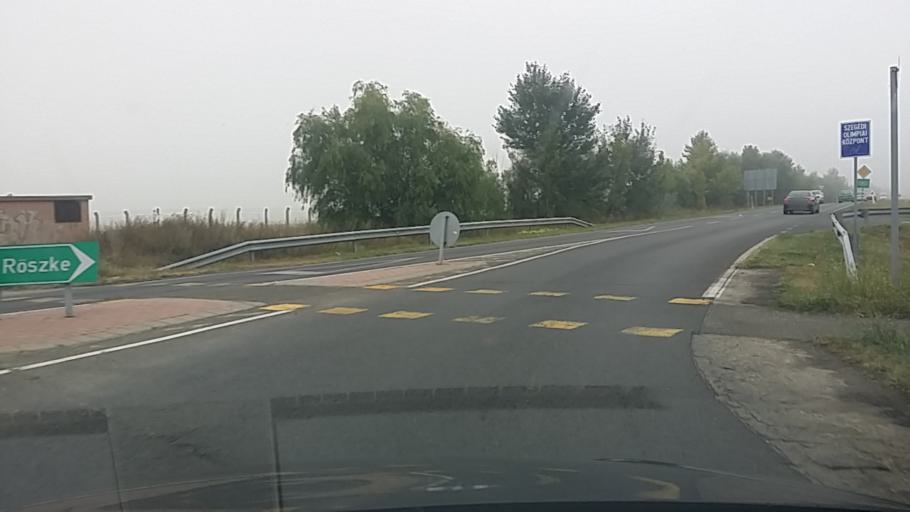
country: HU
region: Csongrad
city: Szeged
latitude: 46.2519
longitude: 20.0817
